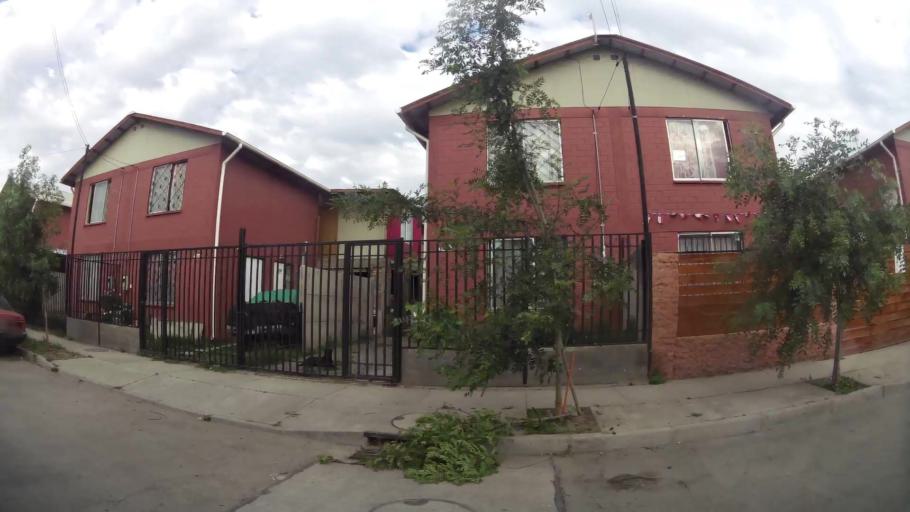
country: CL
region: Santiago Metropolitan
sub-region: Provincia de Cordillera
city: Puente Alto
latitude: -33.6295
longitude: -70.6053
